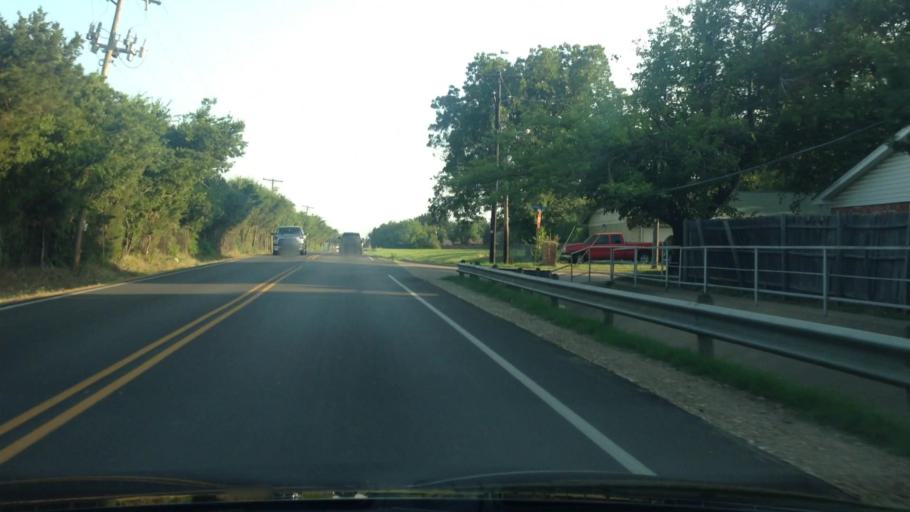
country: US
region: Texas
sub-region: Tarrant County
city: Everman
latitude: 32.6290
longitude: -97.2701
